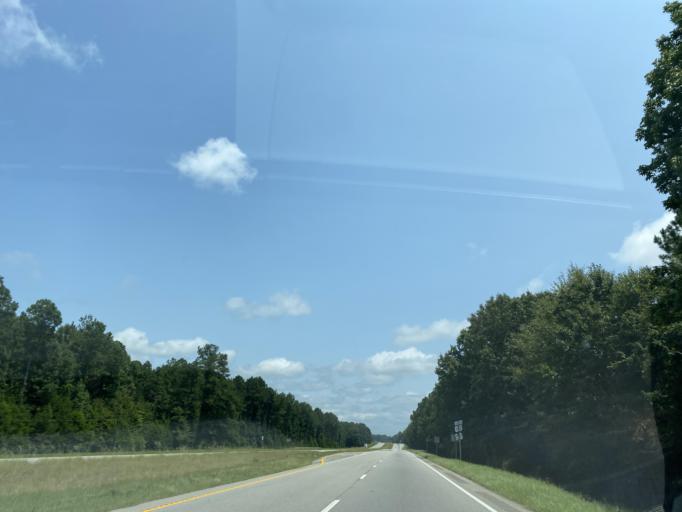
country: US
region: Georgia
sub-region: Telfair County
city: Lumber City
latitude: 31.9066
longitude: -82.6619
